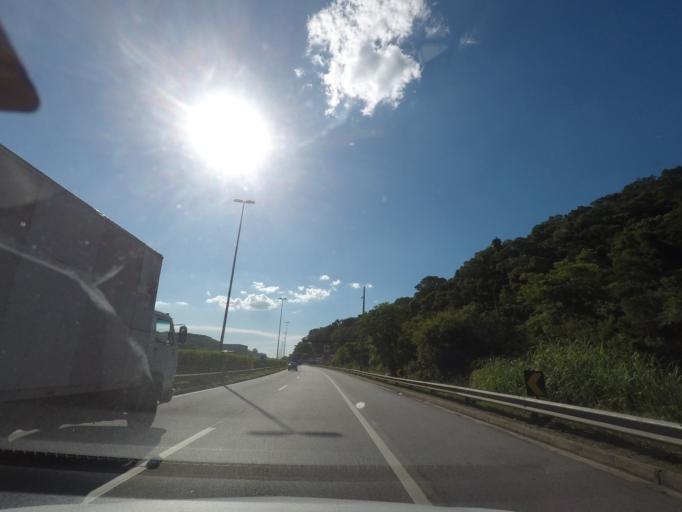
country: BR
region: Rio de Janeiro
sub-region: Petropolis
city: Petropolis
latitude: -22.6538
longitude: -43.1452
